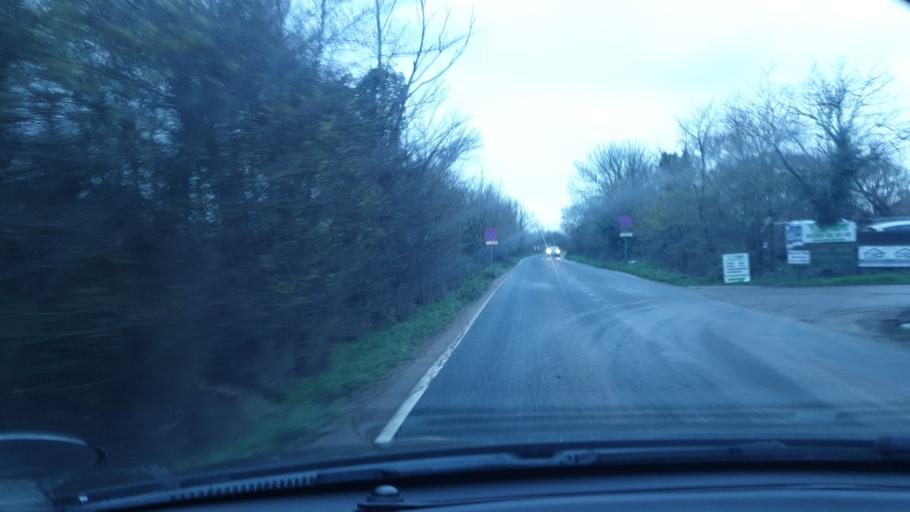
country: GB
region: England
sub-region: Essex
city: Frinton-on-Sea
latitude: 51.8228
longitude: 1.2082
